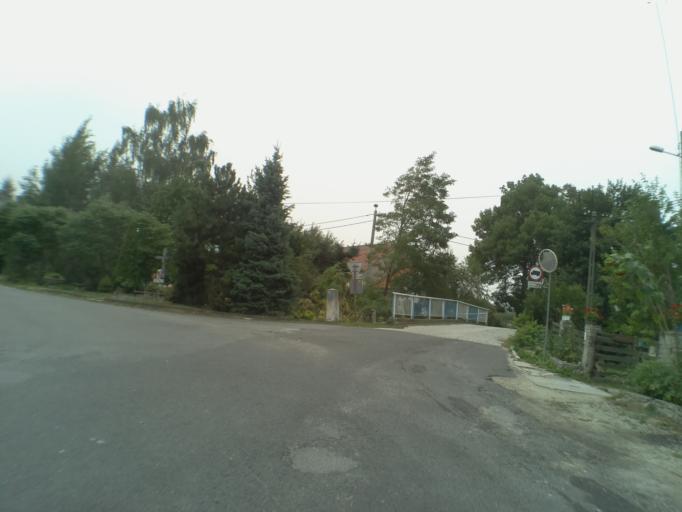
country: PL
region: Lower Silesian Voivodeship
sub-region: Powiat swidnicki
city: Strzegom
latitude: 50.9401
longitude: 16.3276
